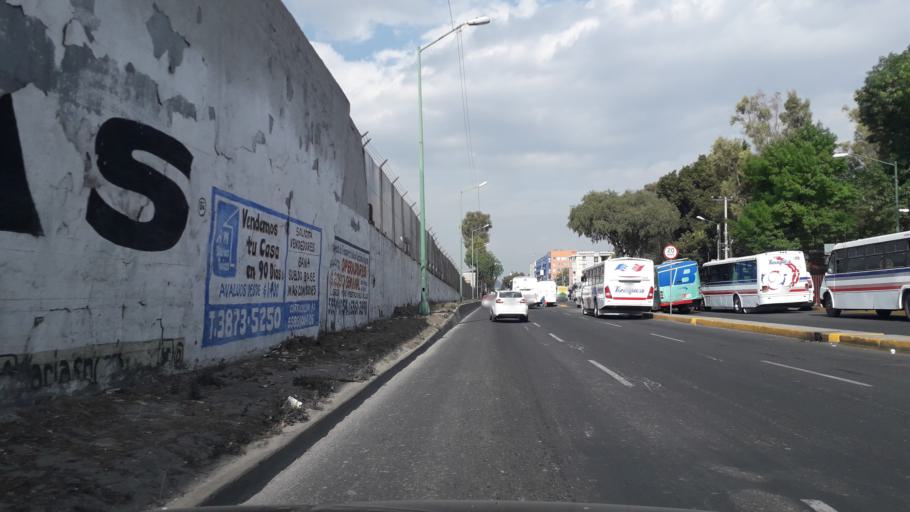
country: MX
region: Mexico City
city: Gustavo A. Madero
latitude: 19.4833
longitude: -99.1055
